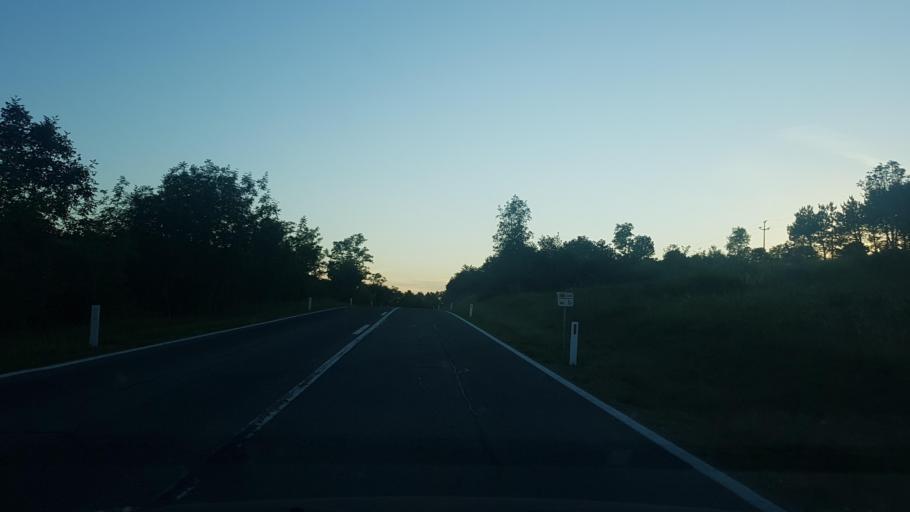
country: SI
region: Divaca
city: Divaca
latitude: 45.7185
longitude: 14.0188
